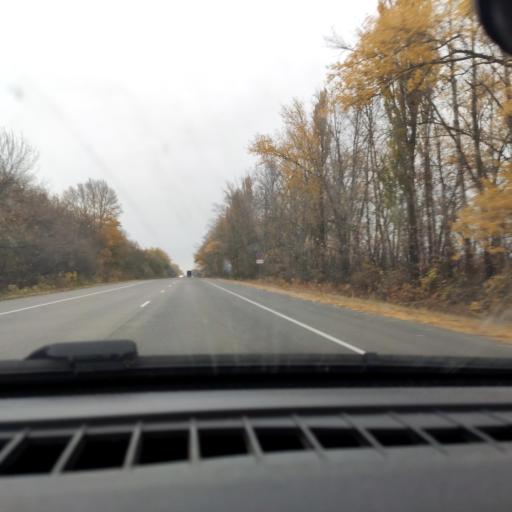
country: RU
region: Voronezj
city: Uryv-Pokrovka
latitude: 51.1650
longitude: 39.0712
